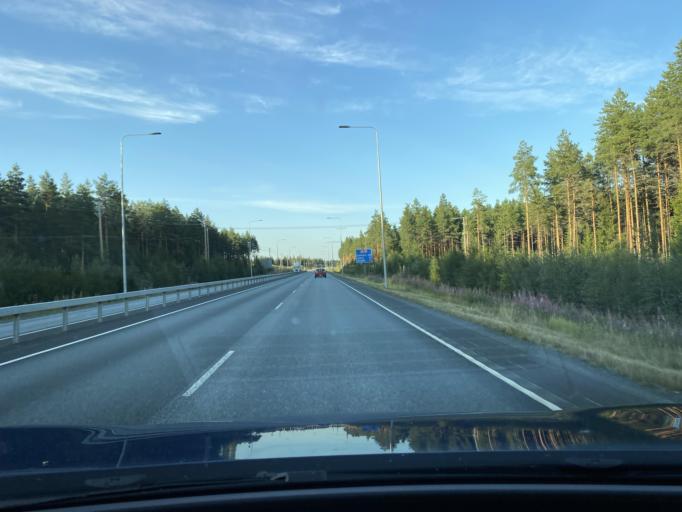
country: FI
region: Southern Ostrobothnia
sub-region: Seinaejoki
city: Seinaejoki
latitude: 62.7290
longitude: 22.8878
